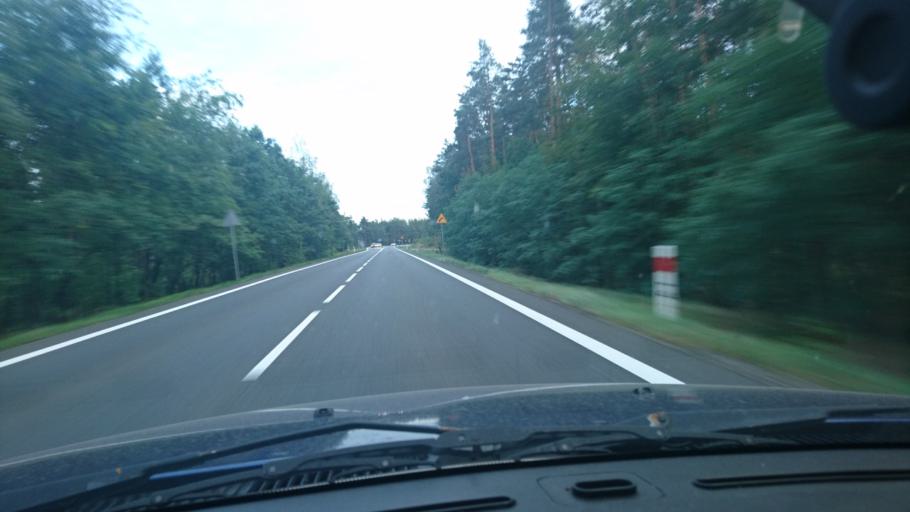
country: PL
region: Silesian Voivodeship
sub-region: Powiat tarnogorski
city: Tworog
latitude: 50.6003
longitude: 18.7017
